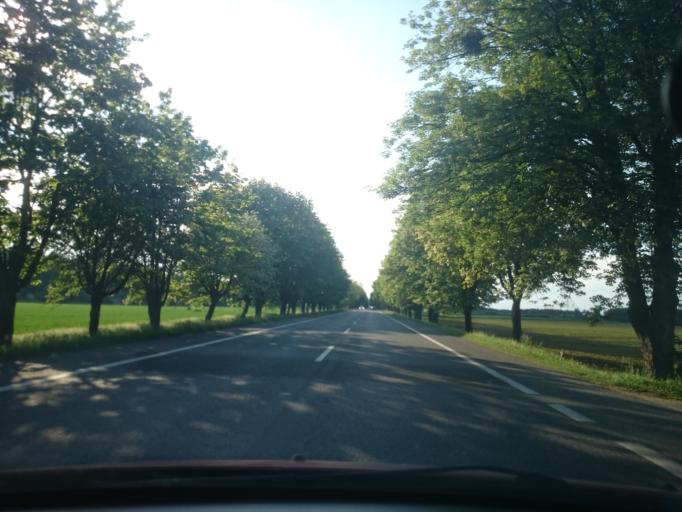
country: PL
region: Opole Voivodeship
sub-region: Powiat strzelecki
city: Strzelce Opolskie
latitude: 50.5393
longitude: 18.2472
